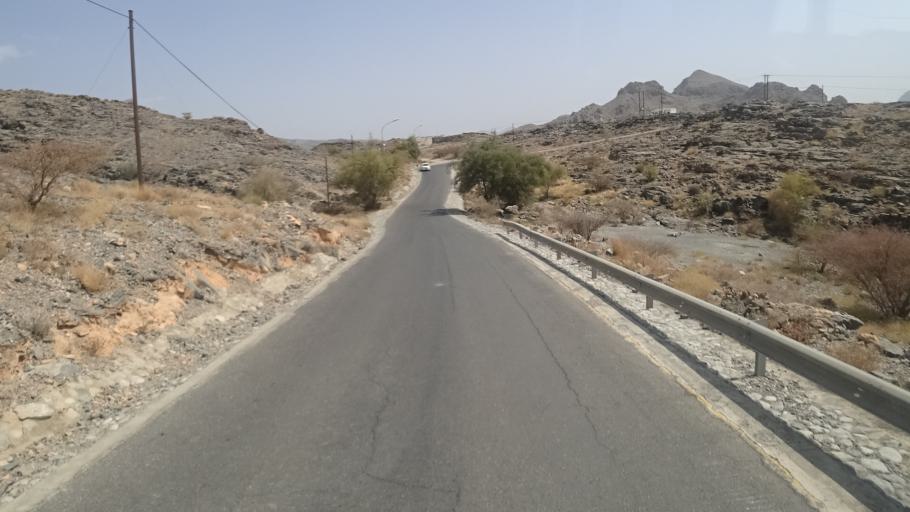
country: OM
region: Muhafazat ad Dakhiliyah
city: Bahla'
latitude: 23.1301
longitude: 57.3048
